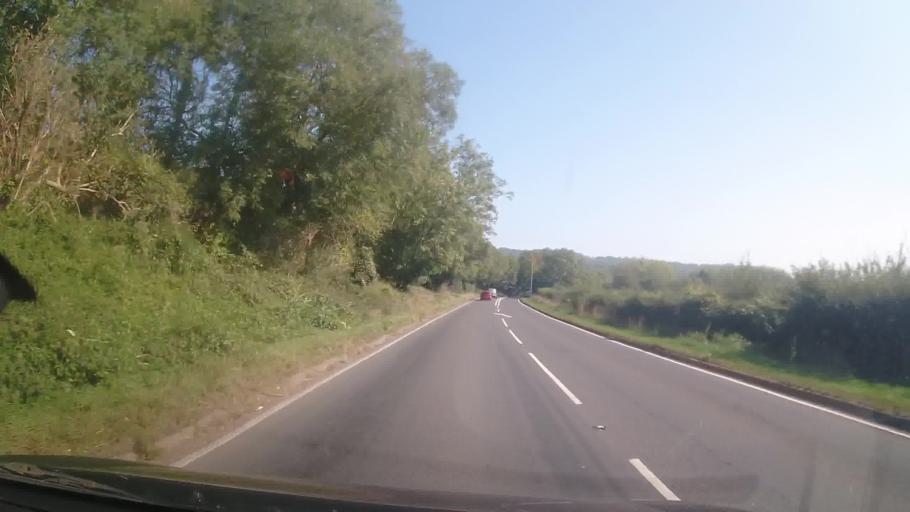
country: GB
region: England
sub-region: Worcestershire
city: Evesham
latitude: 52.1245
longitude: -1.9962
